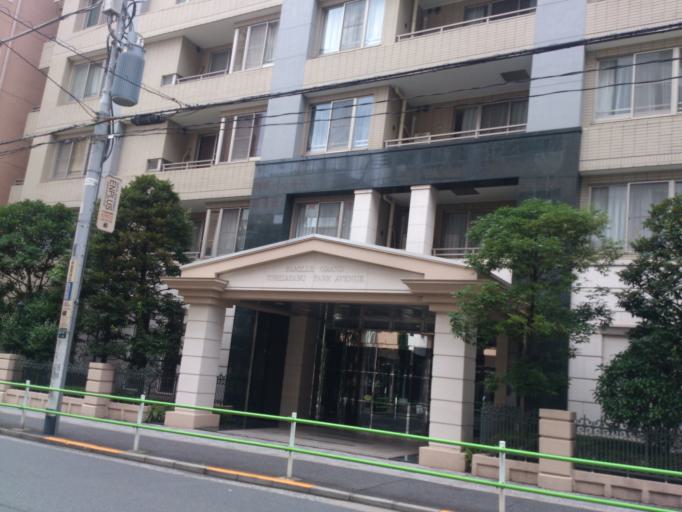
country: JP
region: Tokyo
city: Tokyo
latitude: 35.6551
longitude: 139.7264
